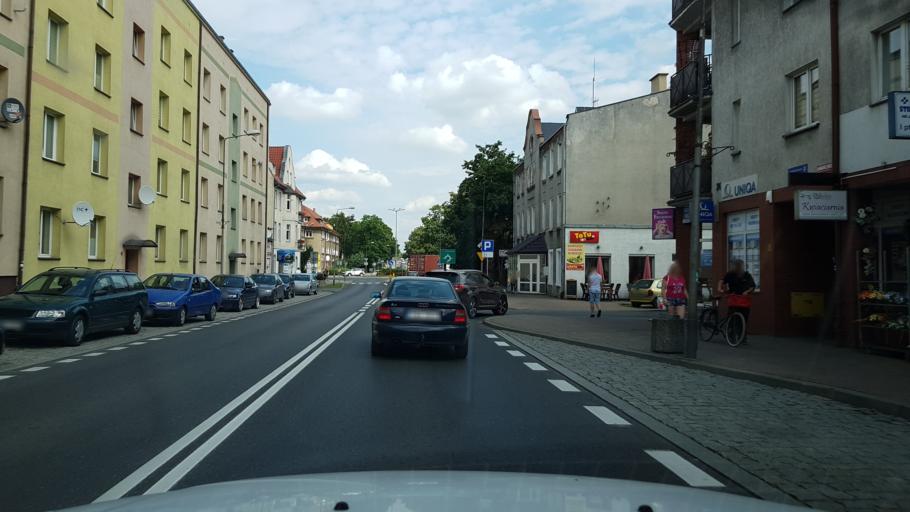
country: PL
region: West Pomeranian Voivodeship
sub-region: Powiat walecki
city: Walcz
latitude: 53.2746
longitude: 16.4783
